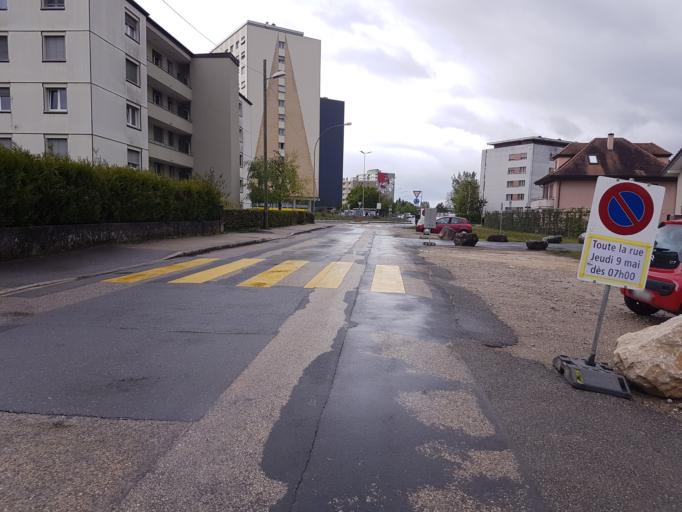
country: CH
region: Vaud
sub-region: Jura-Nord vaudois District
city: Yverdon-les-Bains
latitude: 46.7741
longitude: 6.6322
